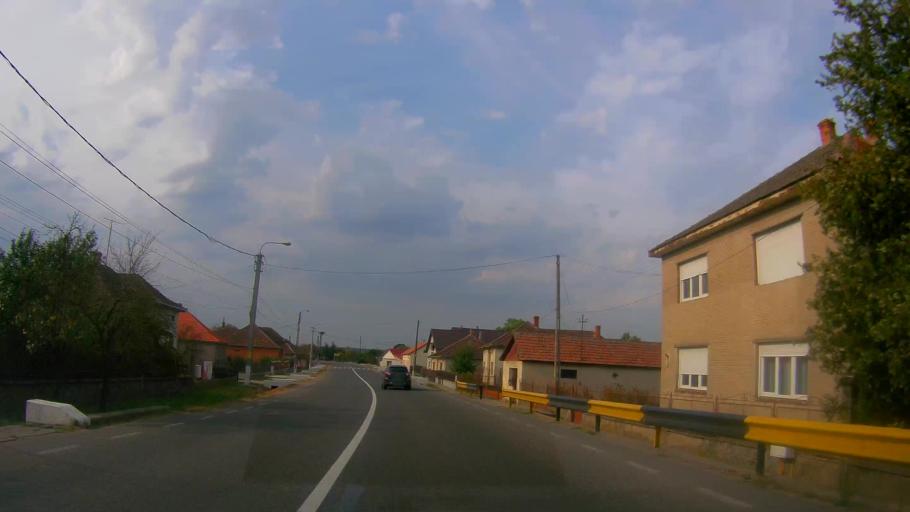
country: RO
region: Satu Mare
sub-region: Oras Ardud
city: Ardud
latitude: 47.6367
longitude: 22.8858
